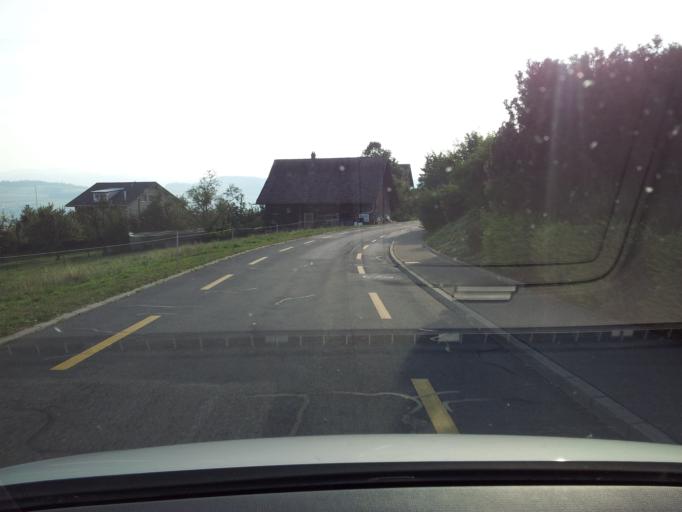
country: CH
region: Lucerne
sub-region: Sursee District
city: Eich
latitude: 47.1596
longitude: 8.1734
